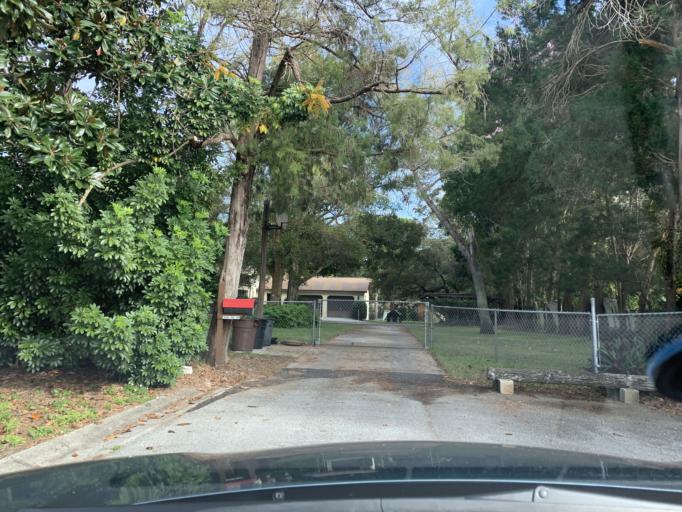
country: US
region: Florida
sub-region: Pinellas County
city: Kenneth City
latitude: 27.8096
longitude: -82.7349
